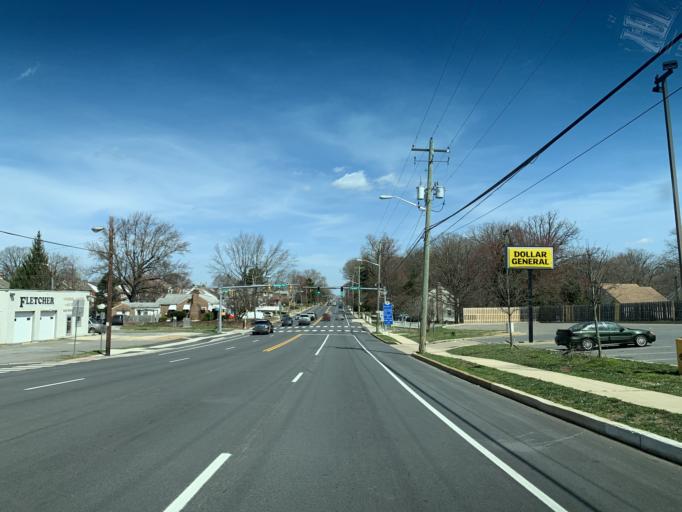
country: US
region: Delaware
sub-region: New Castle County
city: Newport
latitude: 39.7172
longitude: -75.6020
